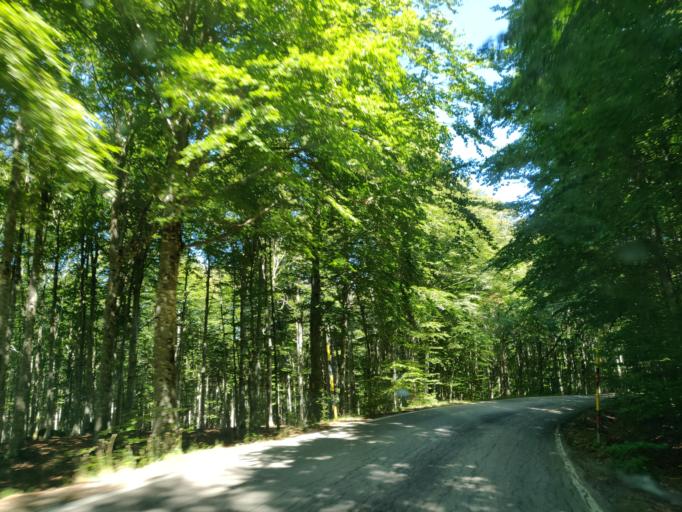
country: IT
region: Tuscany
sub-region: Provincia di Siena
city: Abbadia San Salvatore
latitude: 42.9017
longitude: 11.6165
